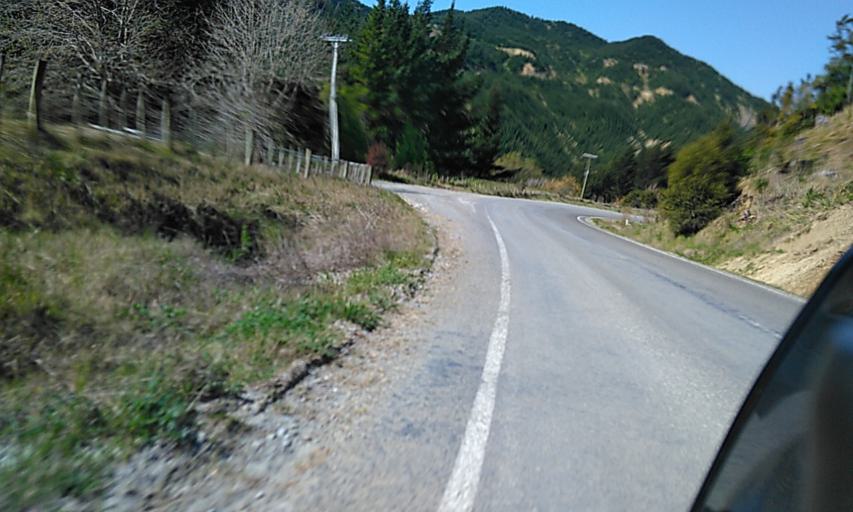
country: NZ
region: Gisborne
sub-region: Gisborne District
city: Gisborne
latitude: -38.3192
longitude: 178.1503
